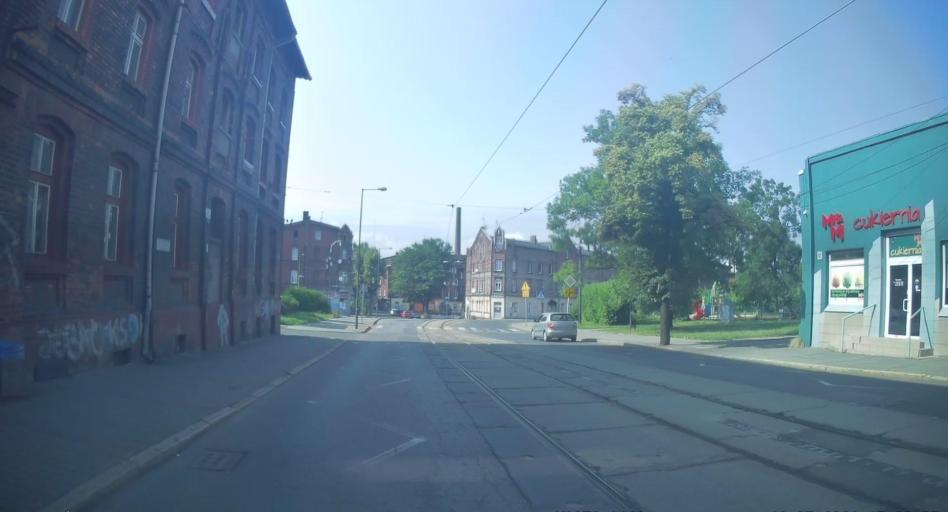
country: PL
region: Silesian Voivodeship
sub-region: Swietochlowice
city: Swietochlowice
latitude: 50.3140
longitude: 18.9132
